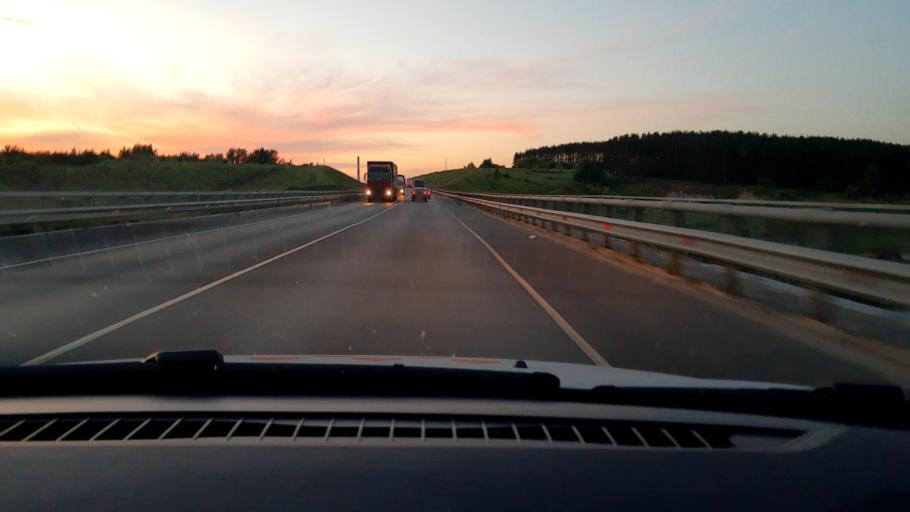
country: RU
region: Nizjnij Novgorod
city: Kstovo
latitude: 56.0780
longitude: 44.1338
